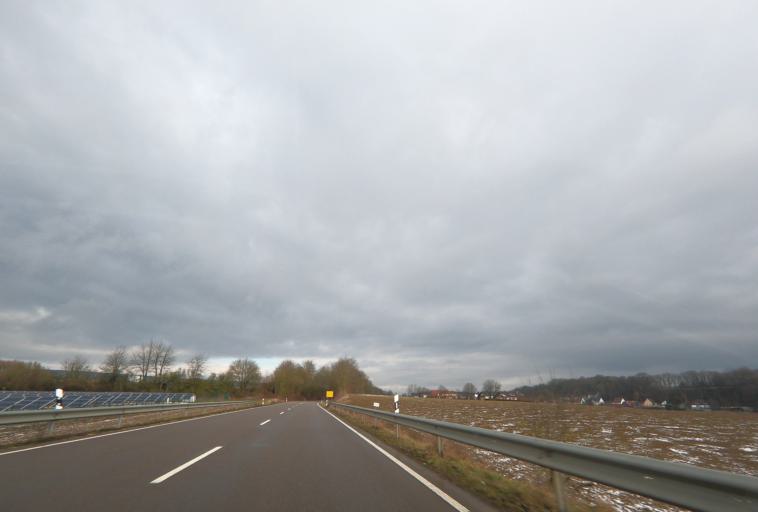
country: DE
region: Bavaria
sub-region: Upper Palatinate
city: Schierling
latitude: 48.8083
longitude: 12.1693
